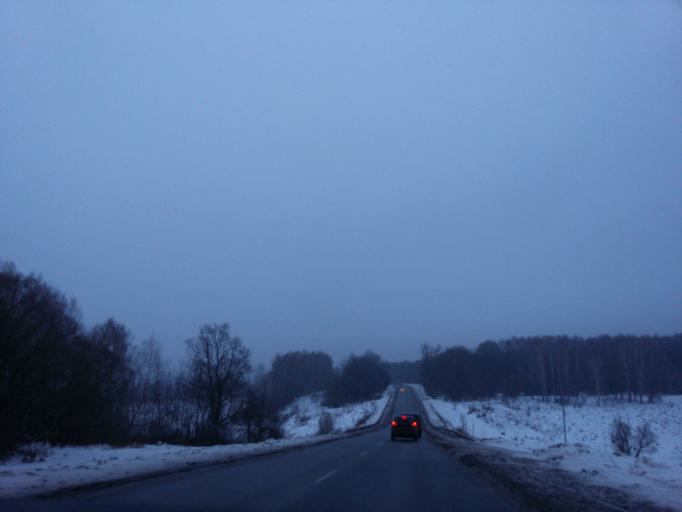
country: RU
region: Tula
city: Pervomayskiy
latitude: 54.0630
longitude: 37.5333
